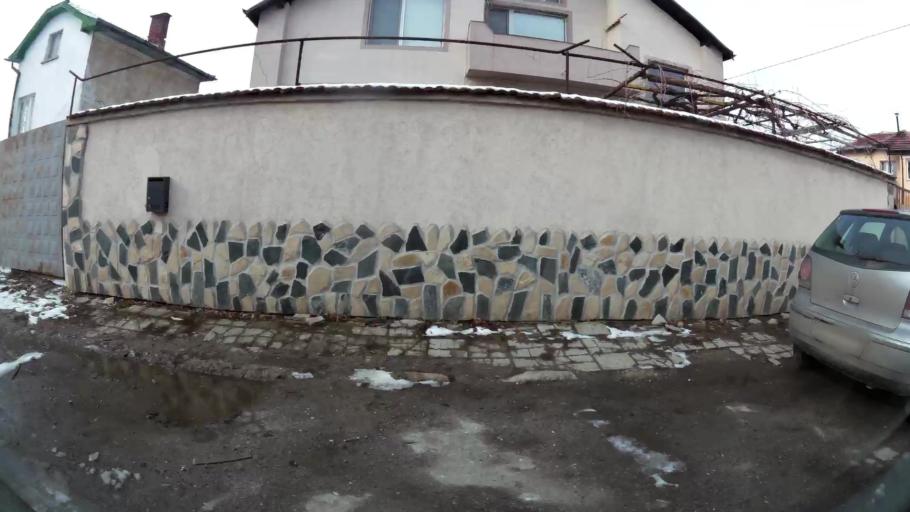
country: BG
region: Sofia-Capital
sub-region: Stolichna Obshtina
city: Sofia
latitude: 42.7131
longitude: 23.4082
